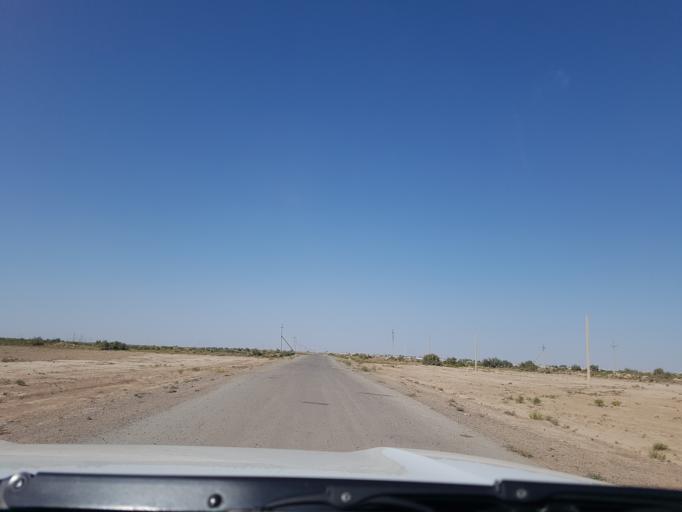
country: IR
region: Razavi Khorasan
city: Sarakhs
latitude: 36.4960
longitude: 61.2538
